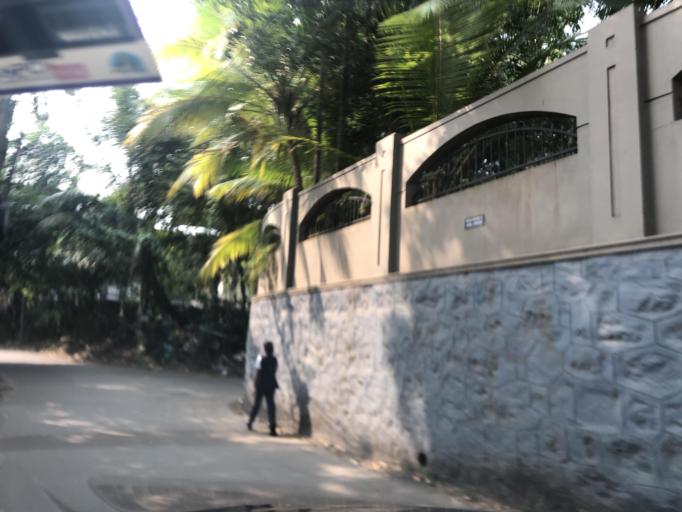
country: IN
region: Kerala
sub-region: Kozhikode
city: Kozhikode
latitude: 11.2786
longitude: 75.7783
